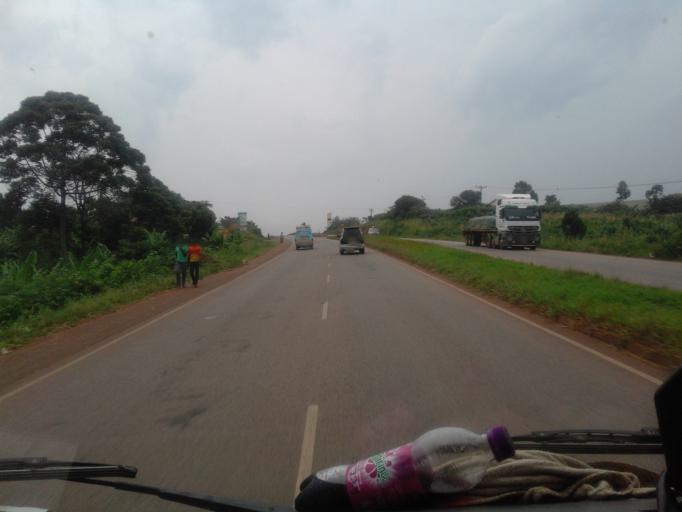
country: UG
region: Eastern Region
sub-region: Jinja District
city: Bugembe
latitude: 0.4774
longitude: 33.2680
